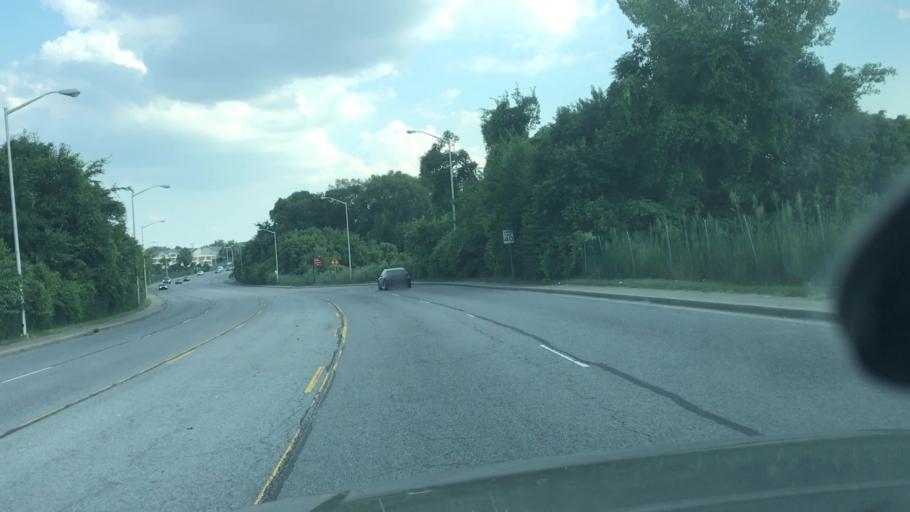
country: US
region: Tennessee
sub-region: Davidson County
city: Nashville
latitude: 36.1757
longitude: -86.8243
